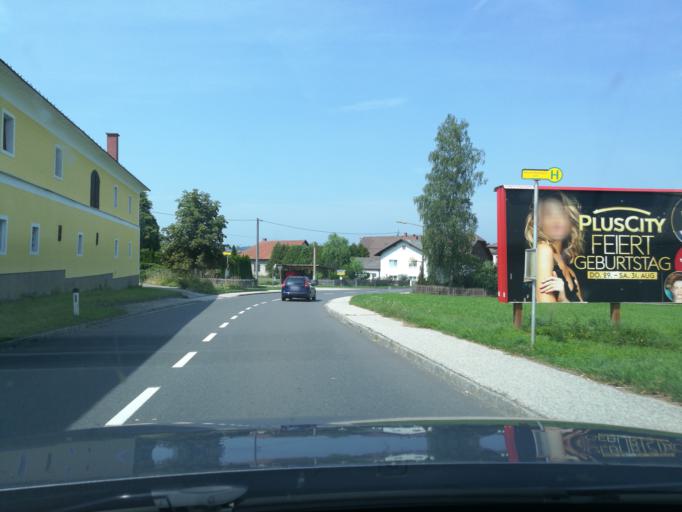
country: AT
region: Upper Austria
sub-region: Politischer Bezirk Grieskirchen
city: Grieskirchen
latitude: 48.3276
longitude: 13.7731
